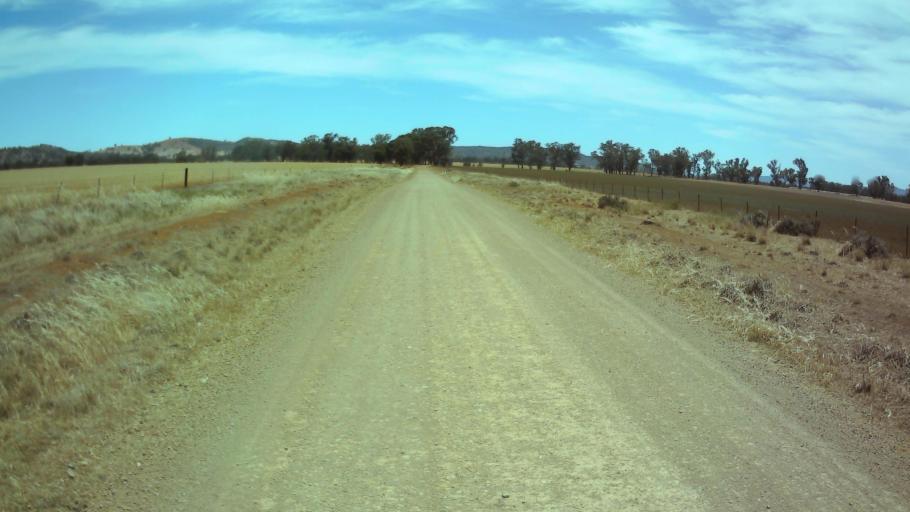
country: AU
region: New South Wales
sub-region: Weddin
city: Grenfell
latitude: -33.7526
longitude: 148.1441
